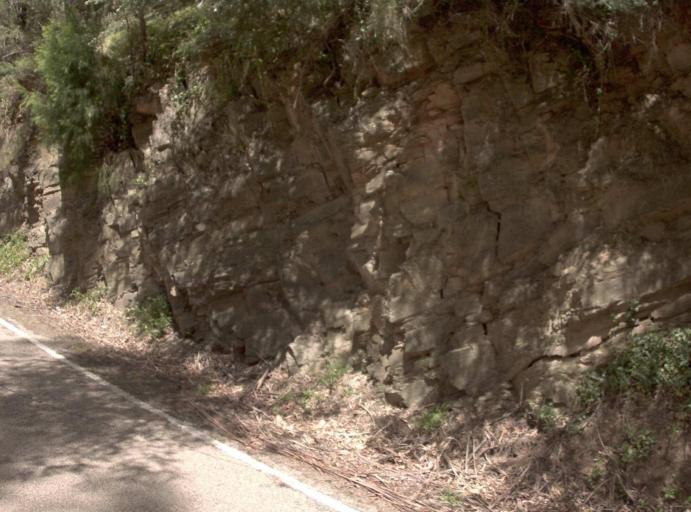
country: AU
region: Victoria
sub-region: East Gippsland
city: Lakes Entrance
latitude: -37.5392
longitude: 147.8646
